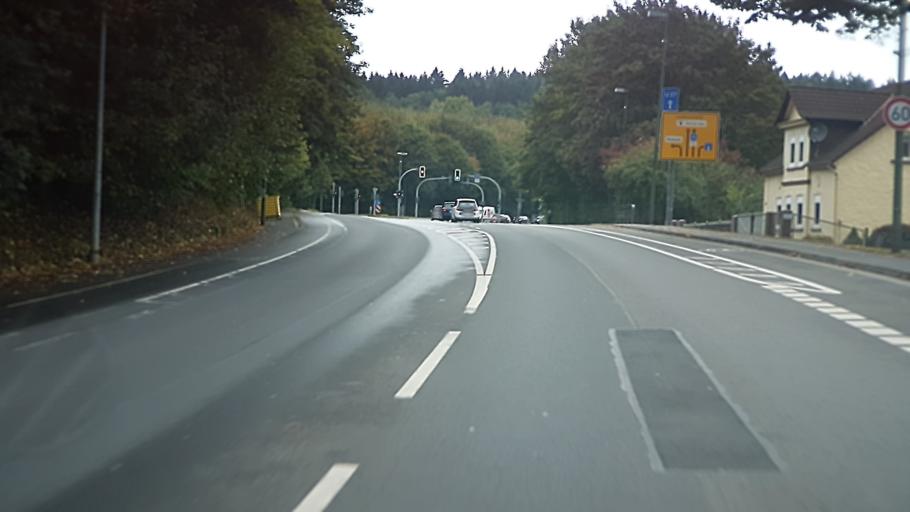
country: DE
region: North Rhine-Westphalia
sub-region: Regierungsbezirk Arnsberg
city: Luedenscheid
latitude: 51.2027
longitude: 7.6558
